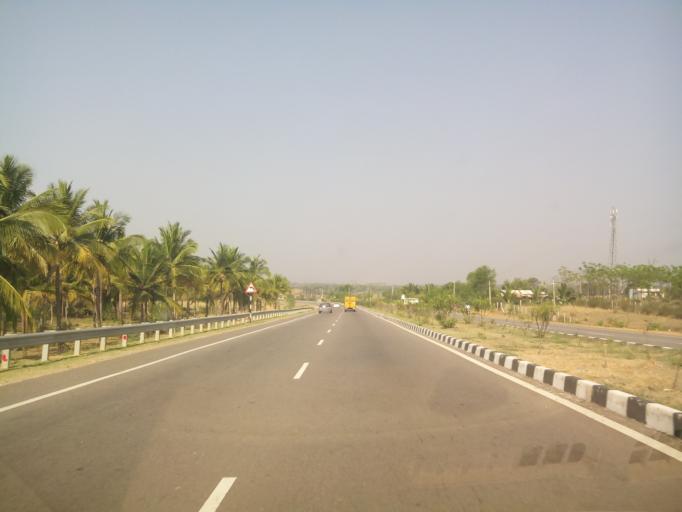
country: IN
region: Karnataka
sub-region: Tumkur
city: Kunigal
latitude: 12.9971
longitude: 76.9153
